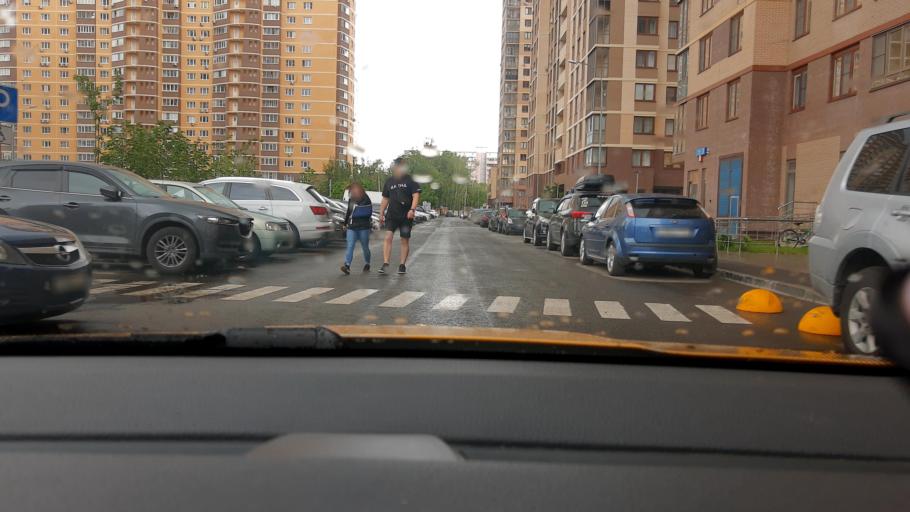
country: RU
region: Moskovskaya
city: Dolgoprudnyy
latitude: 55.9363
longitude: 37.5048
